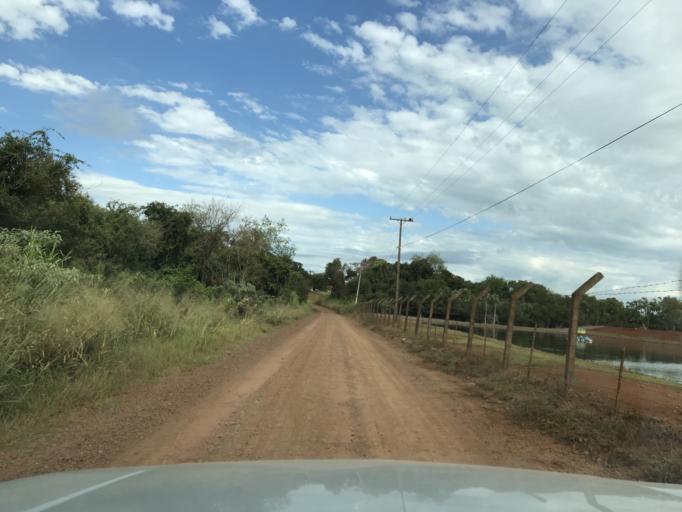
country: BR
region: Parana
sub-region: Palotina
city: Palotina
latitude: -24.3230
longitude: -53.8059
